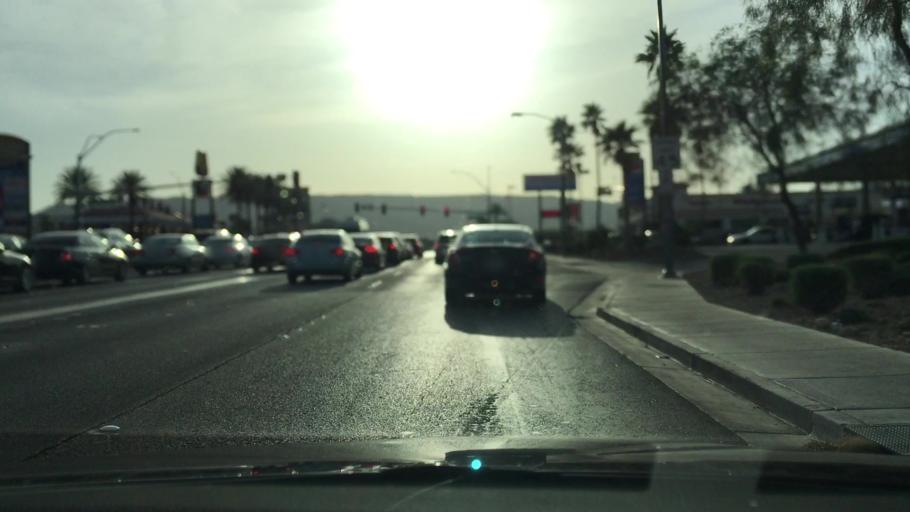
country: US
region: Nevada
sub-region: Clark County
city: Summerlin South
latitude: 36.1002
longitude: -115.2962
